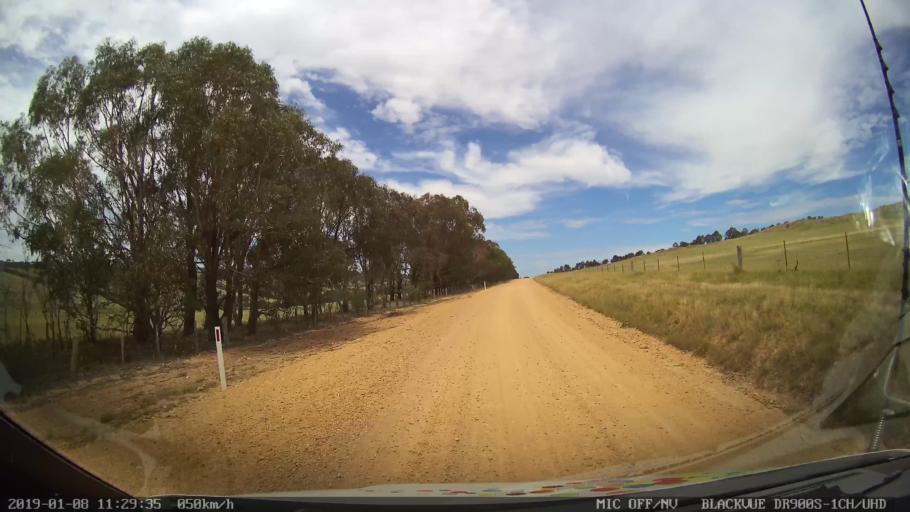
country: AU
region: New South Wales
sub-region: Guyra
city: Guyra
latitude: -30.3014
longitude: 151.5482
